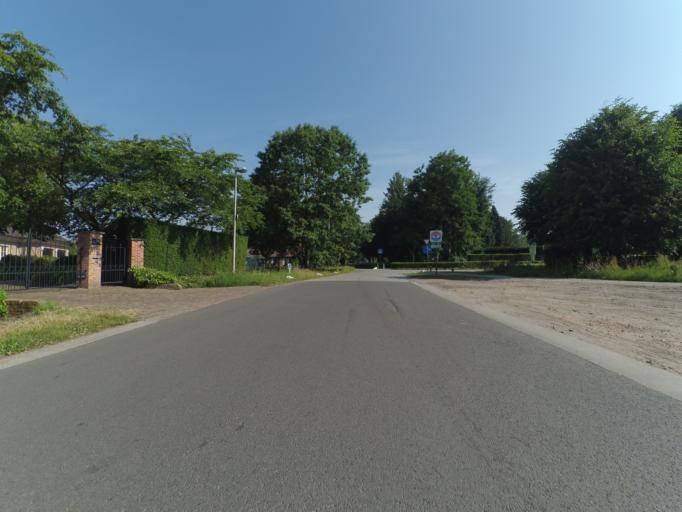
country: BE
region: Flanders
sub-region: Provincie Antwerpen
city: Essen
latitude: 51.4458
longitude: 4.4432
